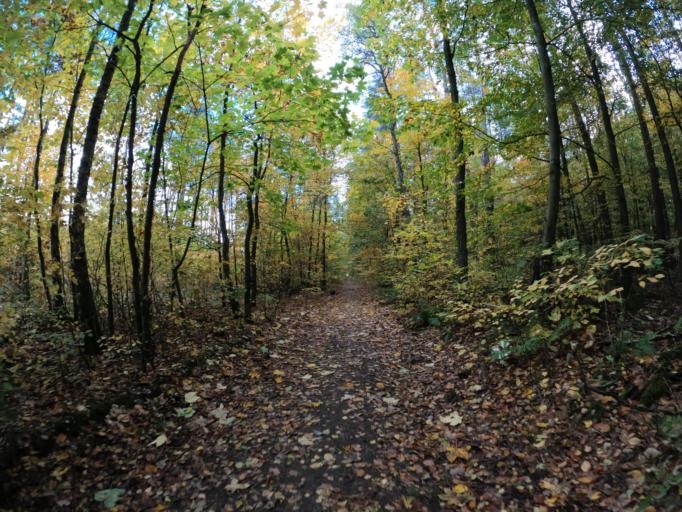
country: PL
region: West Pomeranian Voivodeship
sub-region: Powiat mysliborski
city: Barlinek
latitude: 52.9710
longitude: 15.2527
